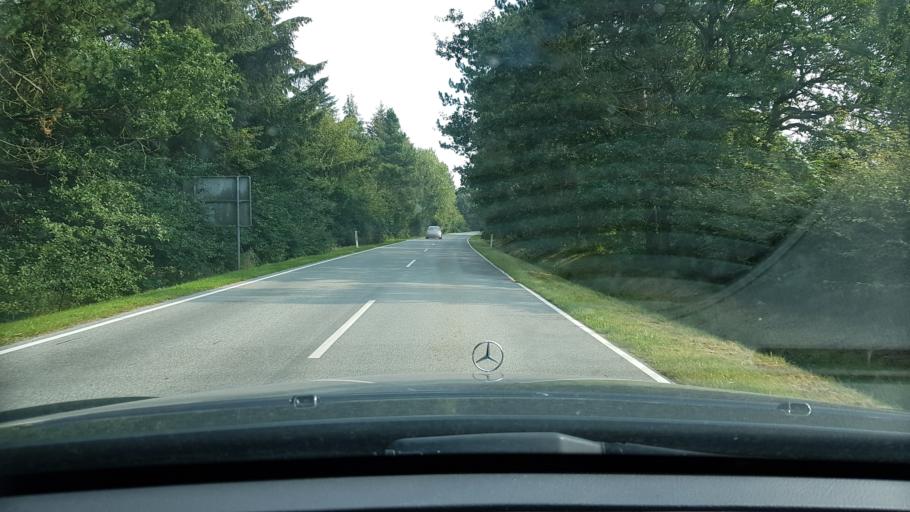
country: DK
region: North Denmark
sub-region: Alborg Kommune
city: Hals
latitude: 56.9001
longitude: 10.2570
